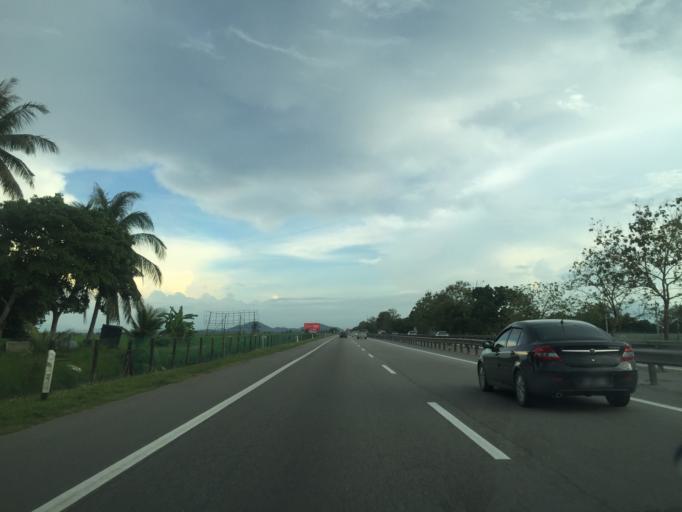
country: MY
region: Kedah
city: Alor Setar
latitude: 6.0083
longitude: 100.4208
